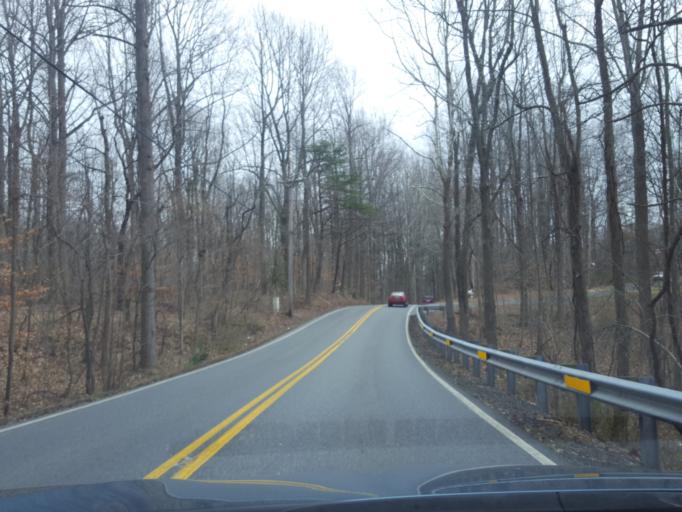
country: US
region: Maryland
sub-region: Calvert County
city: North Beach
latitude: 38.7146
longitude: -76.5583
